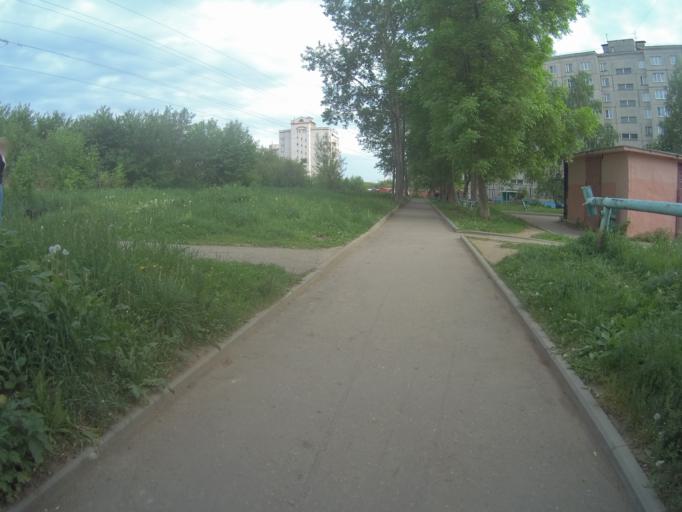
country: RU
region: Vladimir
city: Kommunar
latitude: 56.1619
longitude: 40.4510
